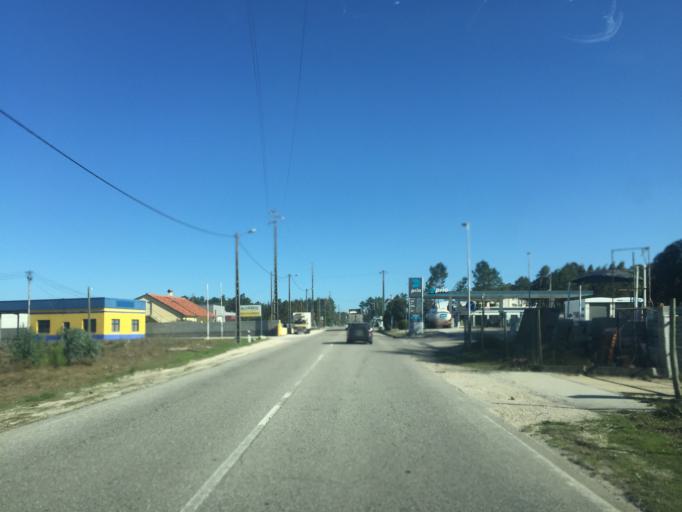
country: PT
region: Leiria
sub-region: Leiria
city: Monte Redondo
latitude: 39.9366
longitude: -8.7978
